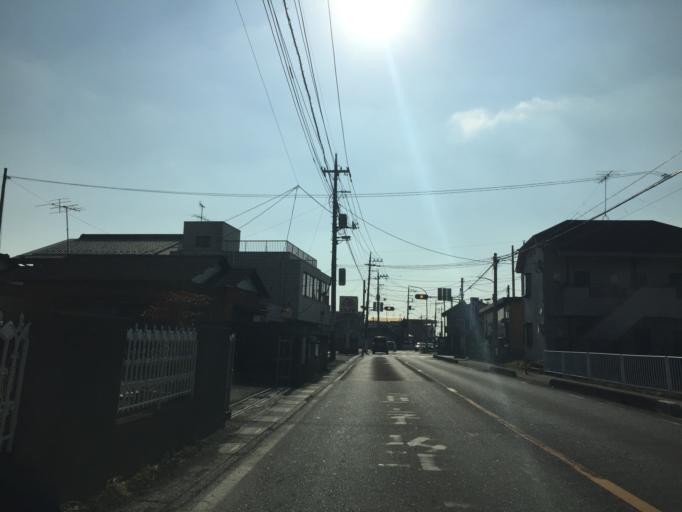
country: JP
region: Saitama
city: Shiki
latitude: 35.8623
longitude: 139.5588
